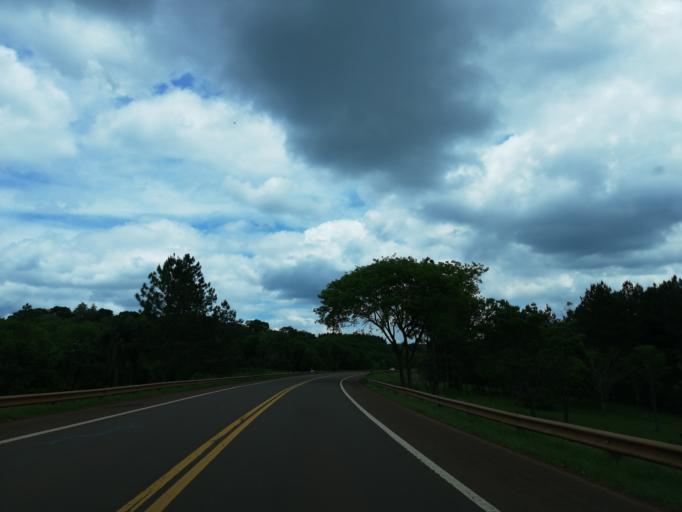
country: AR
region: Misiones
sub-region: Departamento de Leandro N. Alem
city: Leandro N. Alem
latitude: -27.6459
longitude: -55.3554
